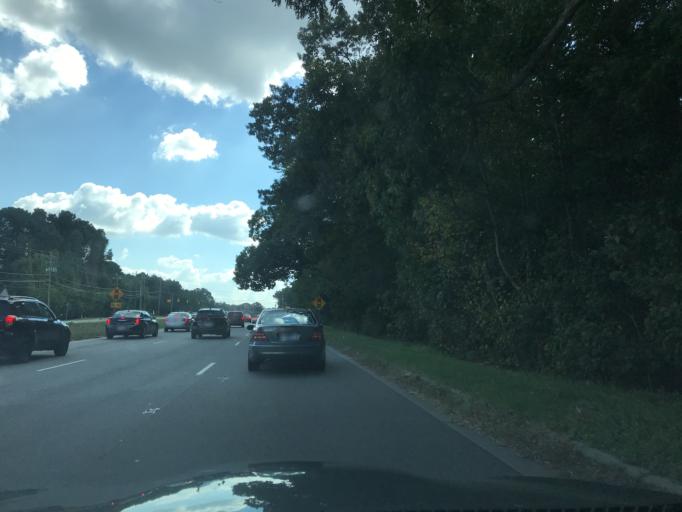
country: US
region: North Carolina
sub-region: Wake County
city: Rolesville
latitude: 35.8707
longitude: -78.5448
